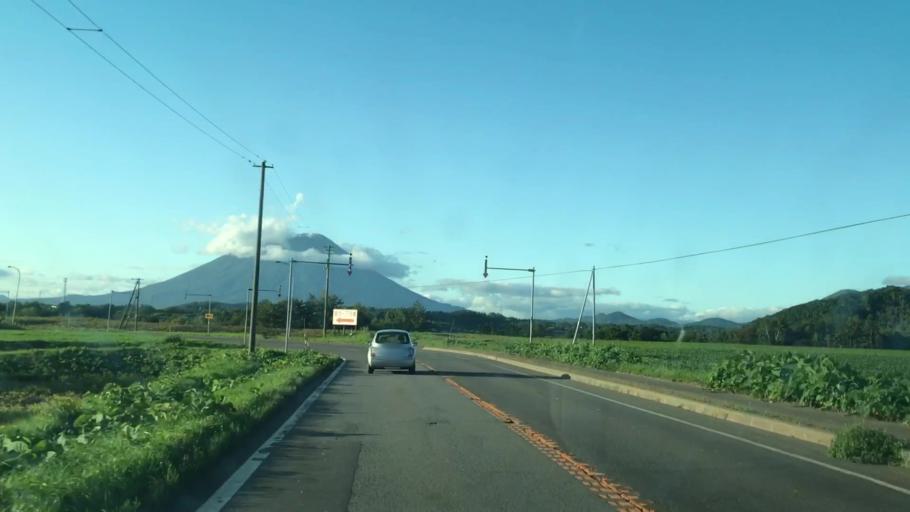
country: JP
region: Hokkaido
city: Niseko Town
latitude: 42.6776
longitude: 140.8417
